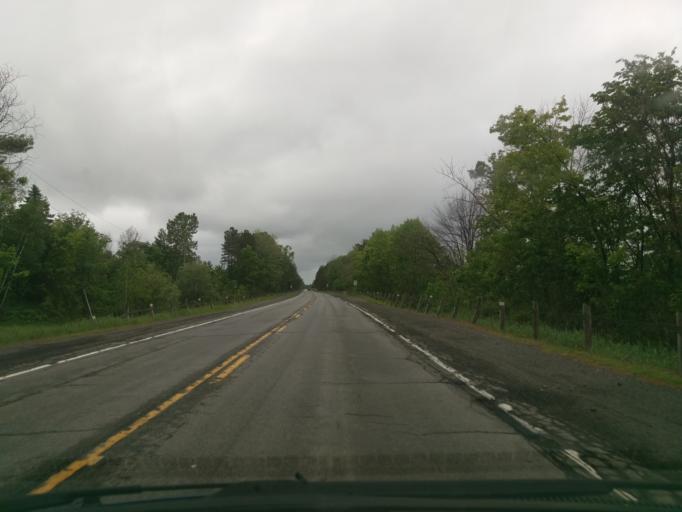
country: CA
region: Ontario
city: Clarence-Rockland
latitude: 45.5198
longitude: -75.3954
